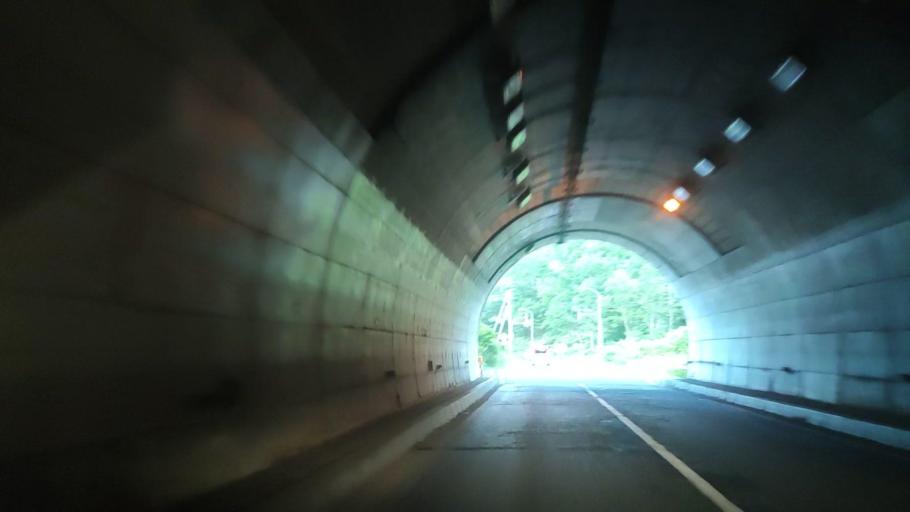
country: JP
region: Hokkaido
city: Bibai
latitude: 43.2908
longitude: 142.0754
